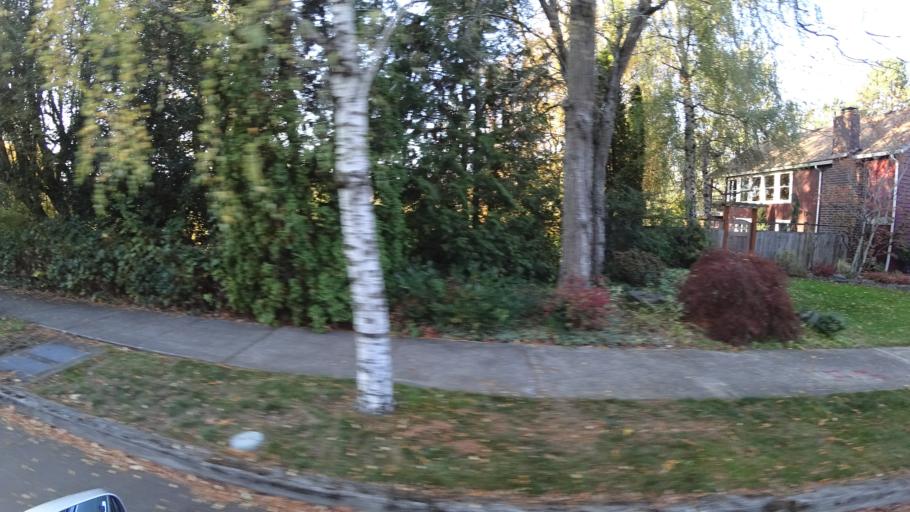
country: US
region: Oregon
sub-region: Multnomah County
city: Gresham
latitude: 45.4940
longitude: -122.4398
